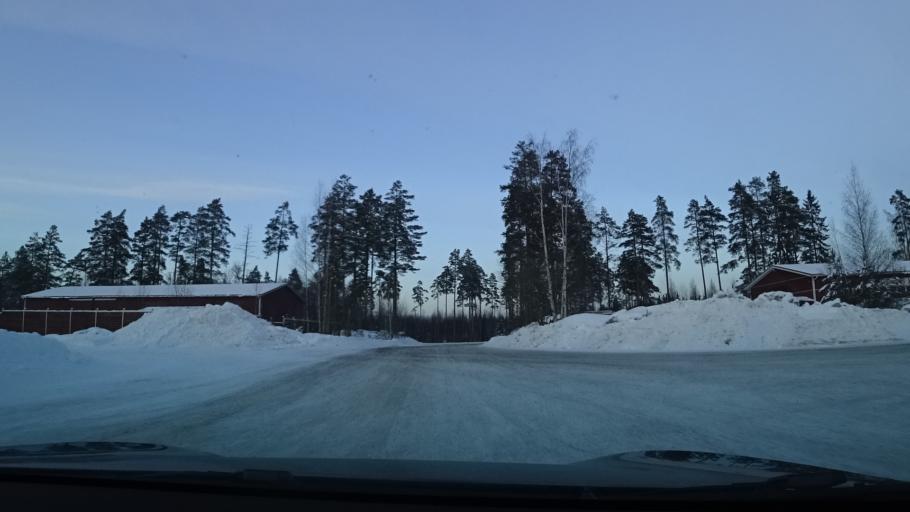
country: FI
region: Kymenlaakso
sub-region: Kotka-Hamina
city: Pyhtaeae
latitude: 60.4897
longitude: 26.5567
